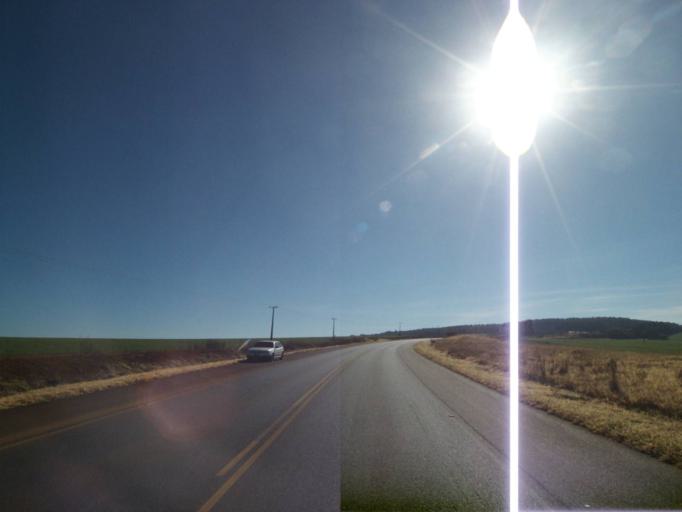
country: BR
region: Parana
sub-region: Tibagi
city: Tibagi
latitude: -24.4404
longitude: -50.4231
